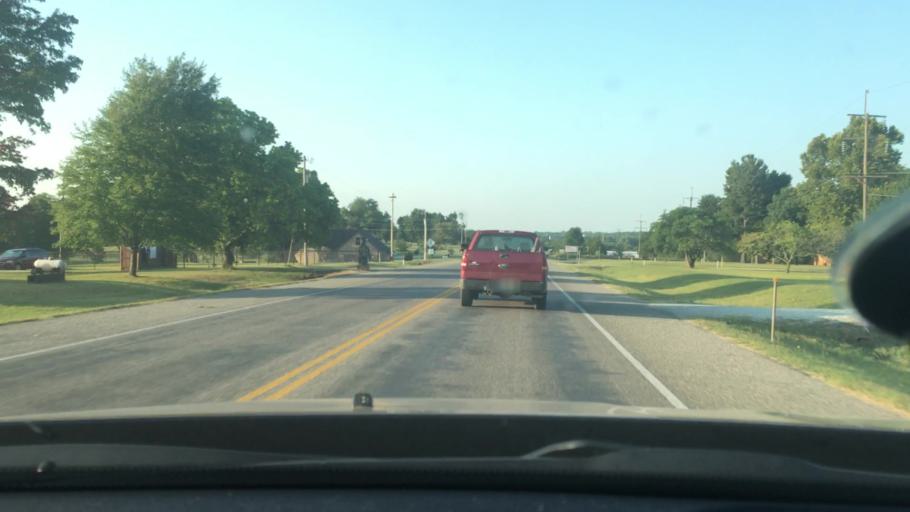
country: US
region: Oklahoma
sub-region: Pontotoc County
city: Byng
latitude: 34.8489
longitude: -96.6786
